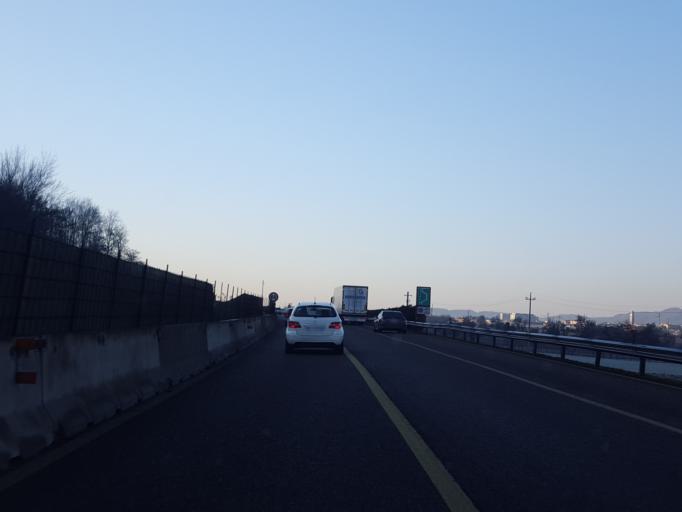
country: IT
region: Veneto
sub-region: Provincia di Vicenza
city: Tavernelle
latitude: 45.5020
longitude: 11.4555
